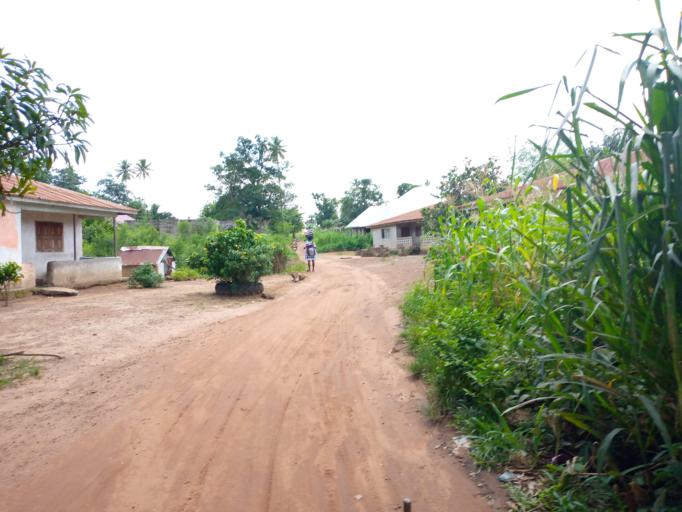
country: SL
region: Northern Province
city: Magburaka
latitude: 8.7090
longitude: -11.9268
